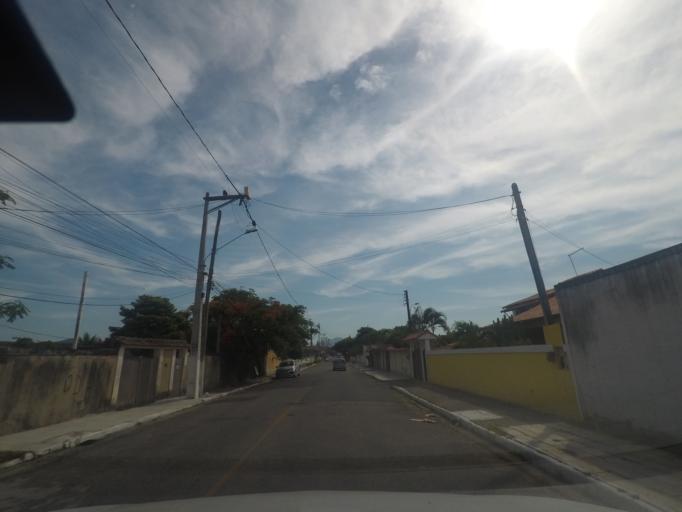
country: BR
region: Rio de Janeiro
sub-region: Marica
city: Marica
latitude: -22.9564
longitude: -42.8137
